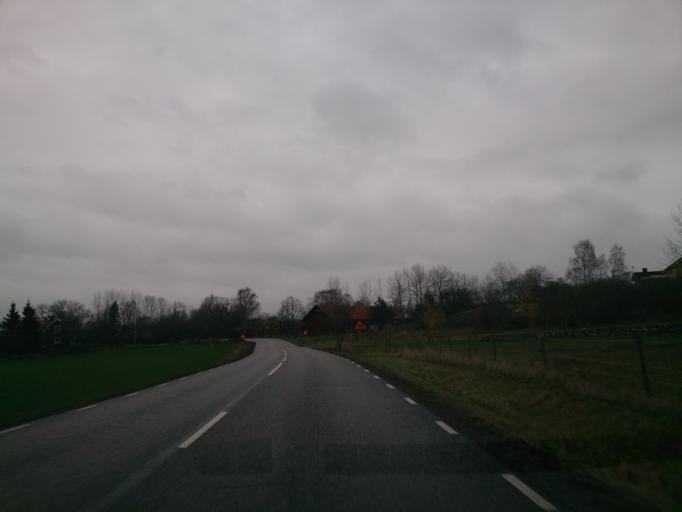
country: SE
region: OEstergoetland
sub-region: Linkopings Kommun
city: Linghem
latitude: 58.4279
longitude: 15.7762
